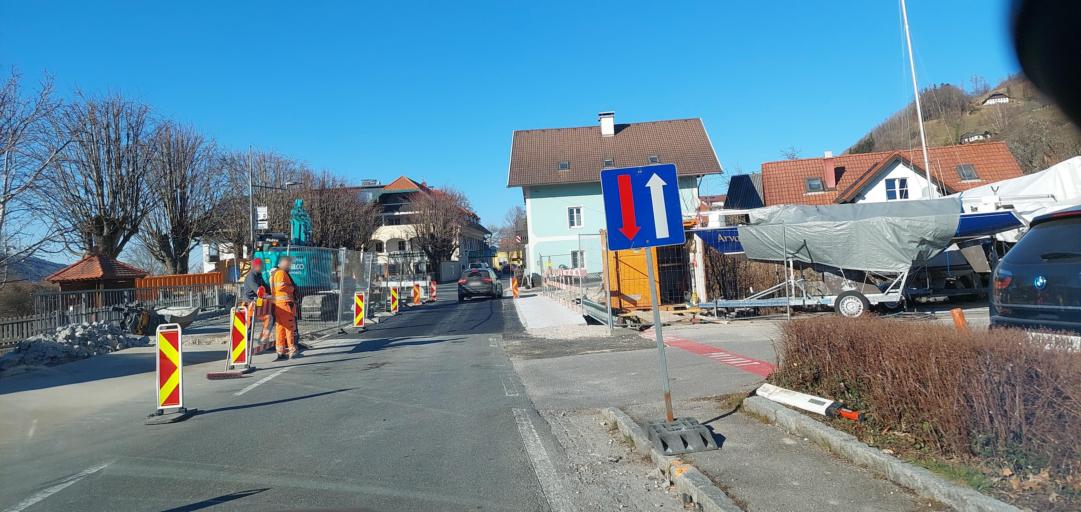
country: AT
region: Upper Austria
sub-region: Politischer Bezirk Vocklabruck
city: Steinbach am Attersee
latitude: 47.8390
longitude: 13.5465
